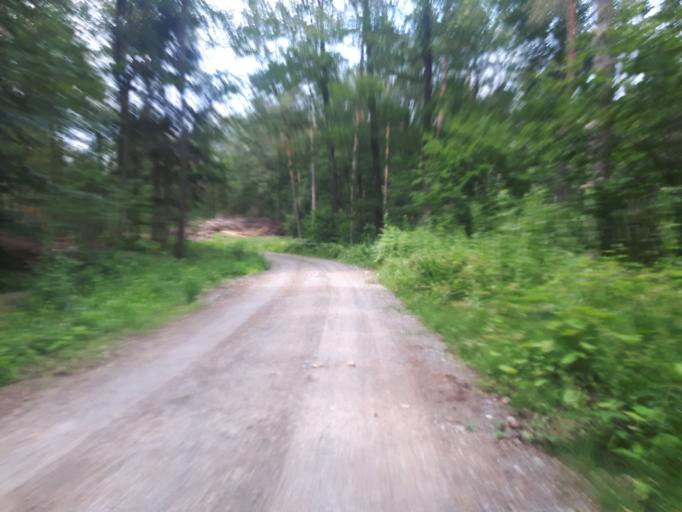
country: DE
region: Baden-Wuerttemberg
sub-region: Regierungsbezirk Stuttgart
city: Cleebronn
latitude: 49.0307
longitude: 9.0203
